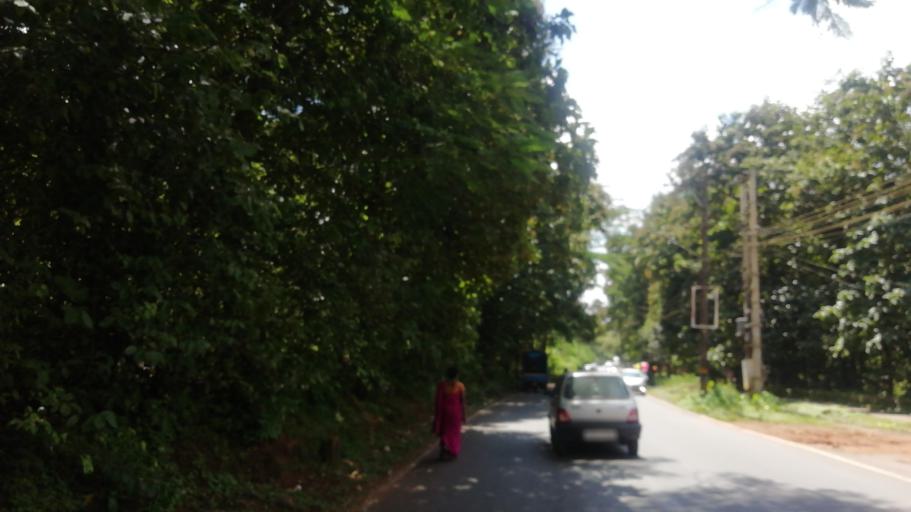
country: IN
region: Goa
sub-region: North Goa
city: Ponda
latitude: 15.3915
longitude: 74.0033
